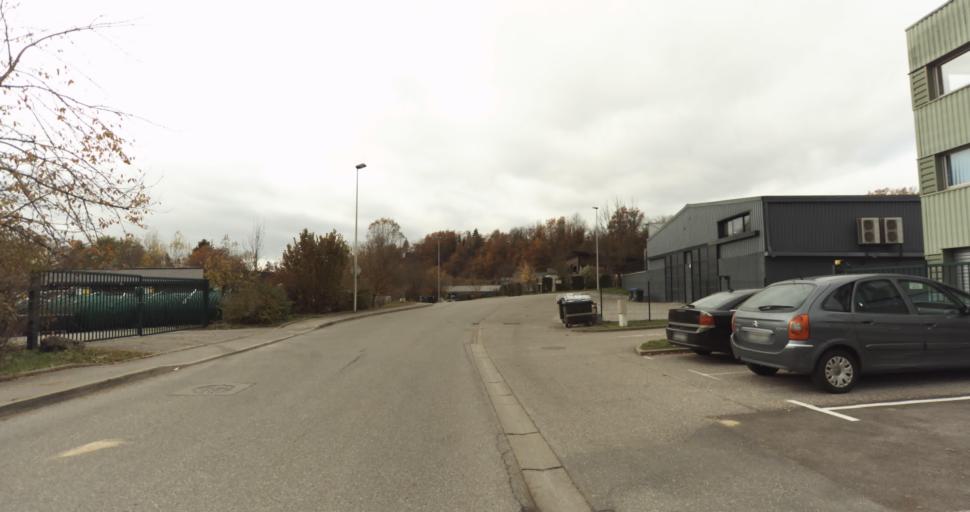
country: FR
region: Rhone-Alpes
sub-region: Departement de la Haute-Savoie
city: Pringy
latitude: 45.9364
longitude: 6.1392
